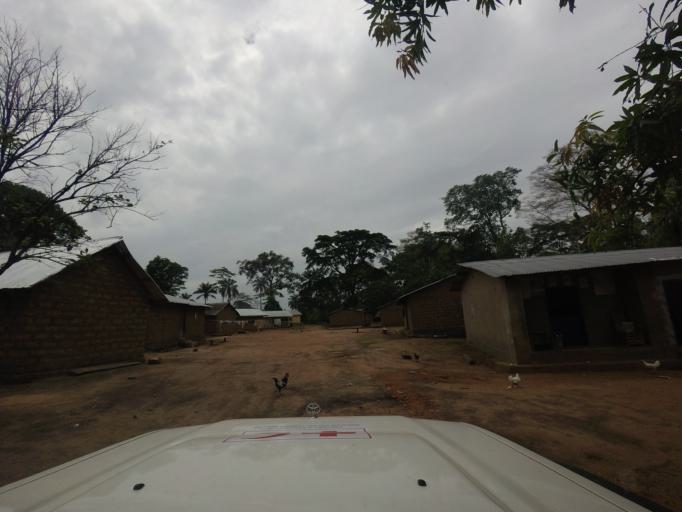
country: SL
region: Eastern Province
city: Buedu
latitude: 8.4213
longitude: -10.2652
